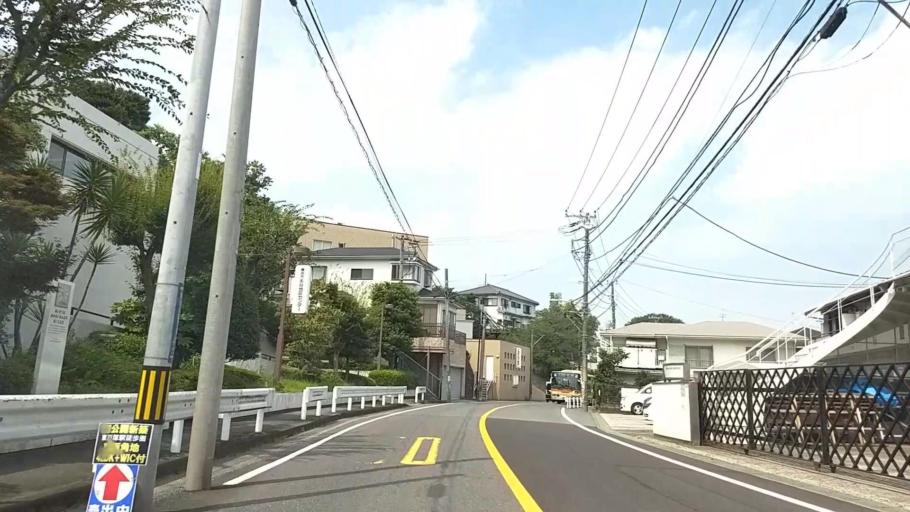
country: JP
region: Kanagawa
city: Yokohama
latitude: 35.4170
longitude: 139.5647
